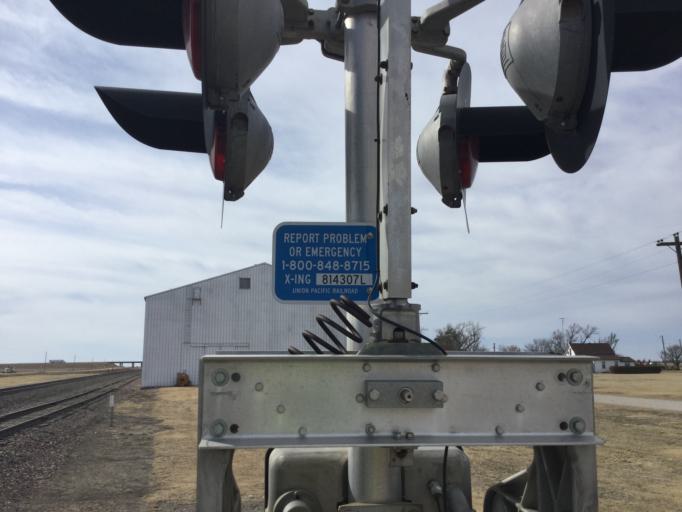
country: US
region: Kansas
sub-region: Ellis County
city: Victoria
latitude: 38.8676
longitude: -99.0770
